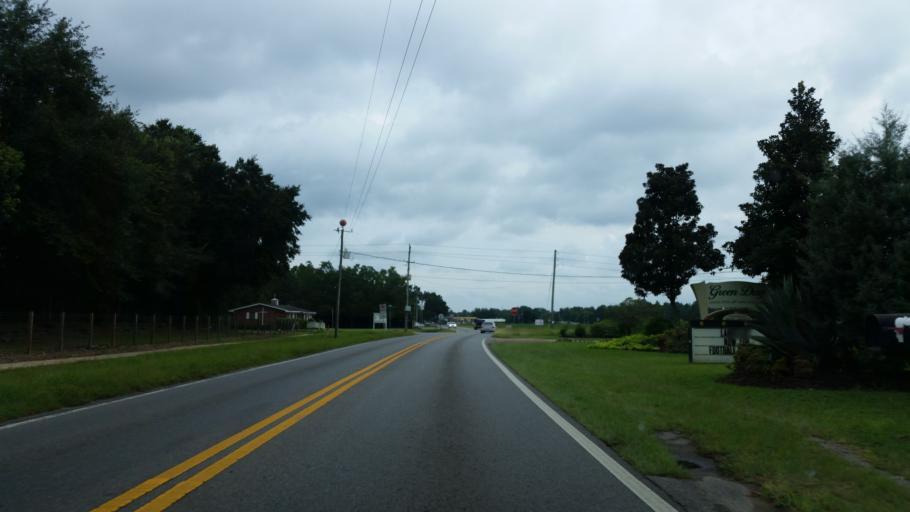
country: US
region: Florida
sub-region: Santa Rosa County
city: Pace
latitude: 30.6193
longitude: -87.1484
